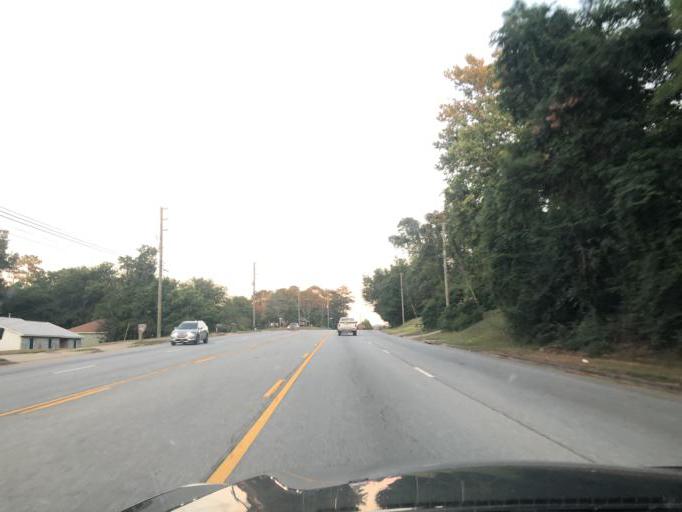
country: US
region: Georgia
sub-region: Muscogee County
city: Columbus
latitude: 32.4645
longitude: -84.8978
